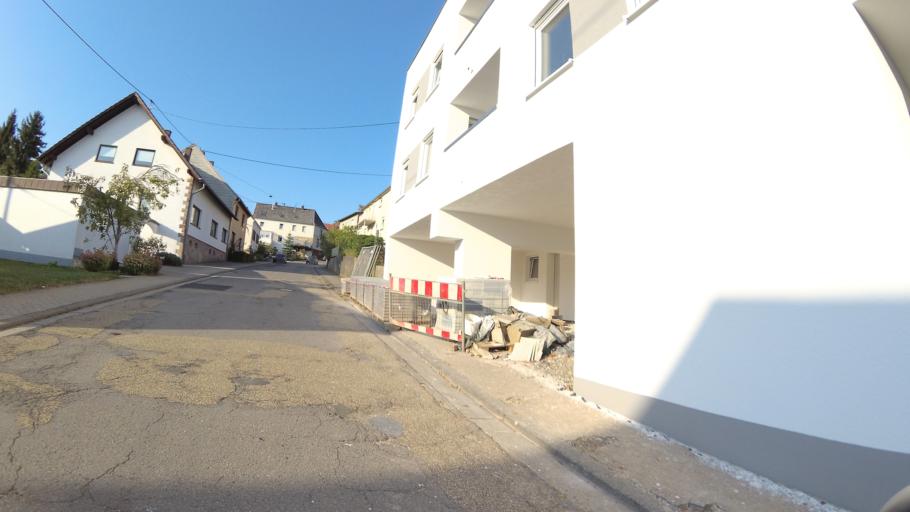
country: DE
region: Saarland
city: Sankt Ingbert
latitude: 49.2181
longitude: 7.1546
